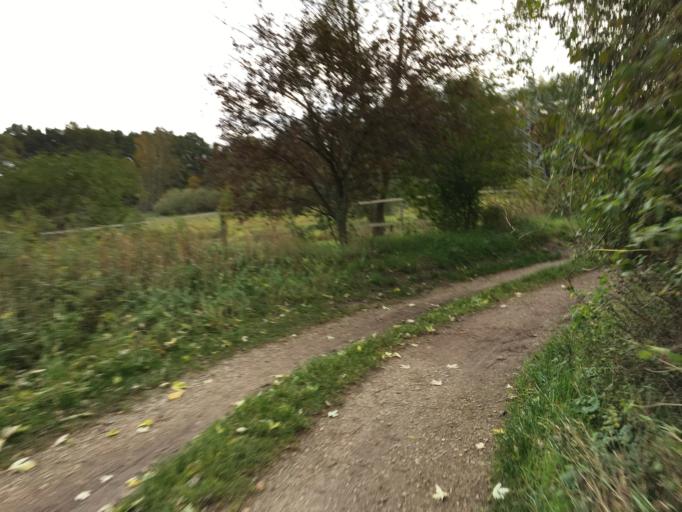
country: DE
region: Lower Saxony
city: Braunschweig
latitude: 52.2982
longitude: 10.5353
